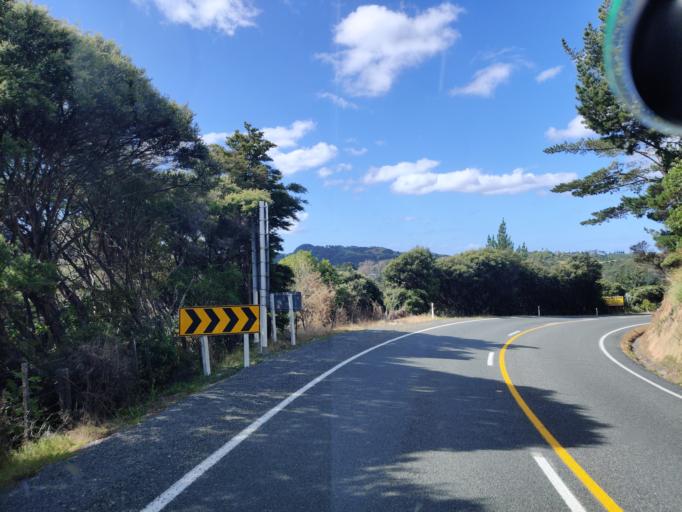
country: NZ
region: Northland
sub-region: Whangarei
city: Ngunguru
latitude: -35.6150
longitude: 174.5209
